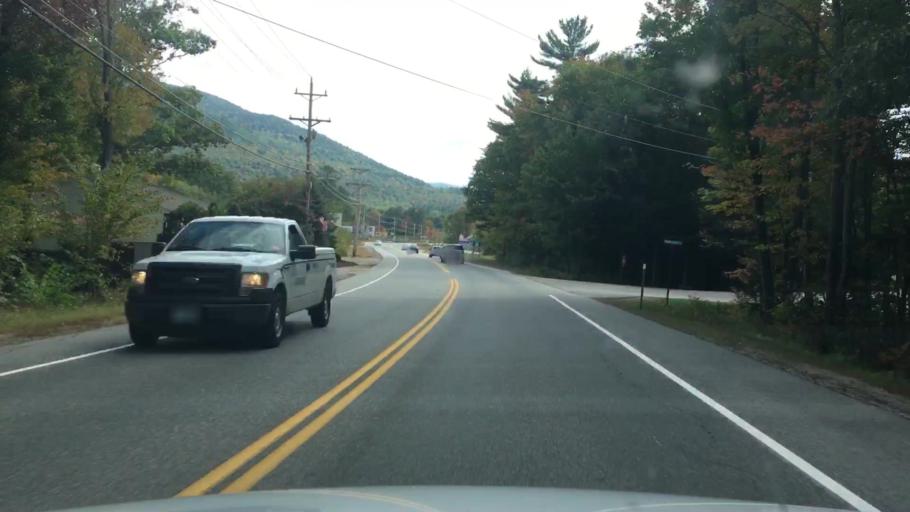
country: US
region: New Hampshire
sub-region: Carroll County
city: North Conway
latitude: 44.1090
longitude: -71.1637
